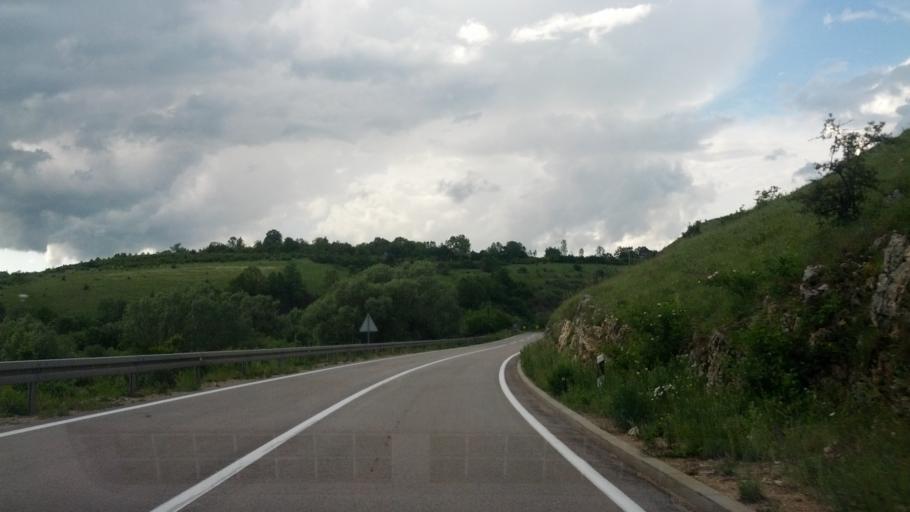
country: BA
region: Federation of Bosnia and Herzegovina
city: Izacic
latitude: 44.9178
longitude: 15.7141
